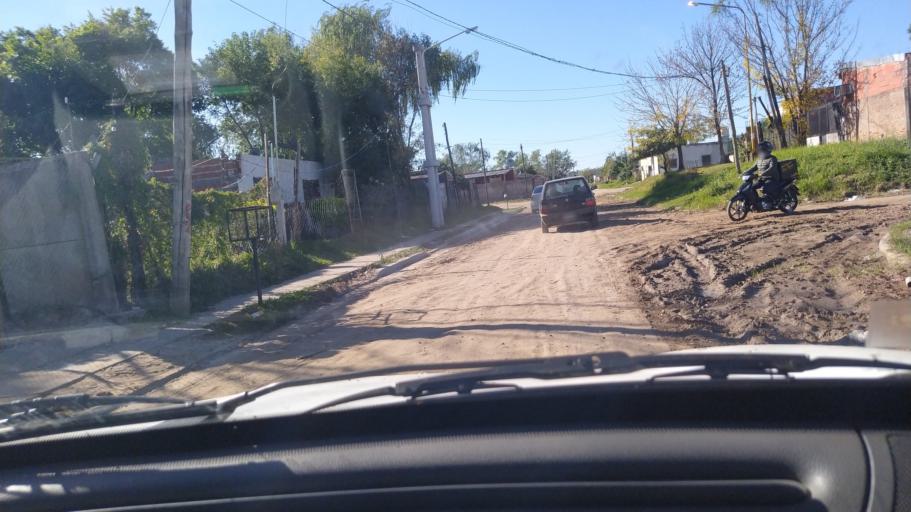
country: AR
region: Corrientes
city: Corrientes
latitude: -27.5006
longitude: -58.8021
